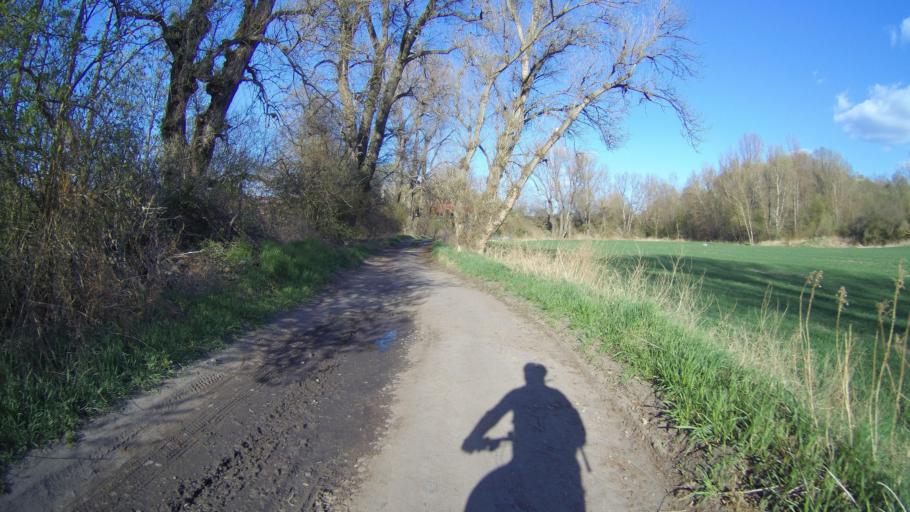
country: CZ
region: Ustecky
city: Zatec
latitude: 50.3333
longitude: 13.5611
